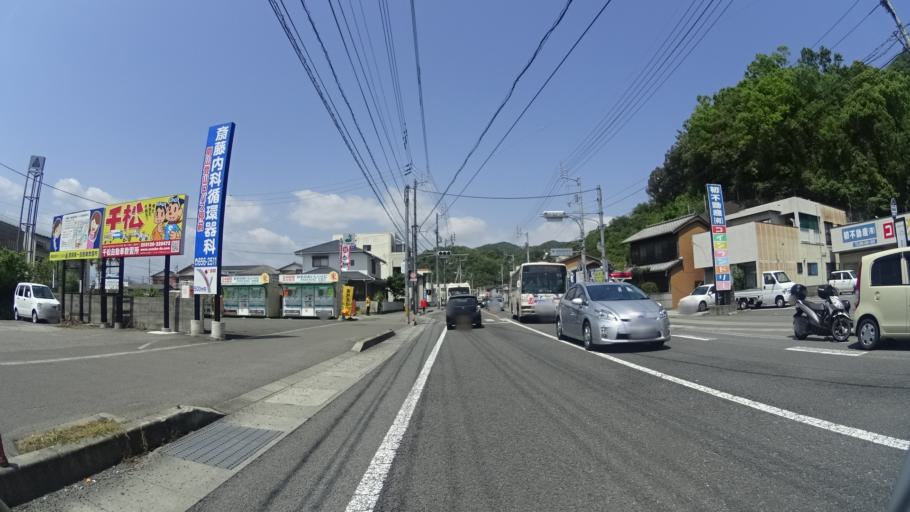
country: JP
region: Tokushima
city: Tokushima-shi
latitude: 34.0560
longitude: 134.5432
